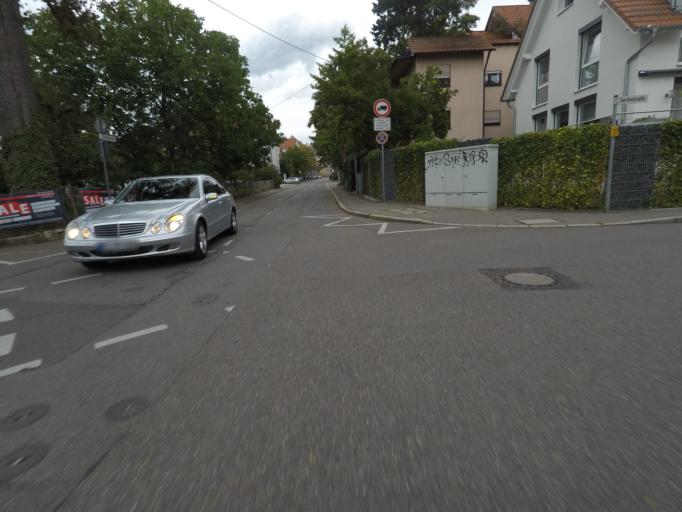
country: DE
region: Baden-Wuerttemberg
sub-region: Regierungsbezirk Stuttgart
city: Leinfelden-Echterdingen
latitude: 48.6868
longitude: 9.1683
